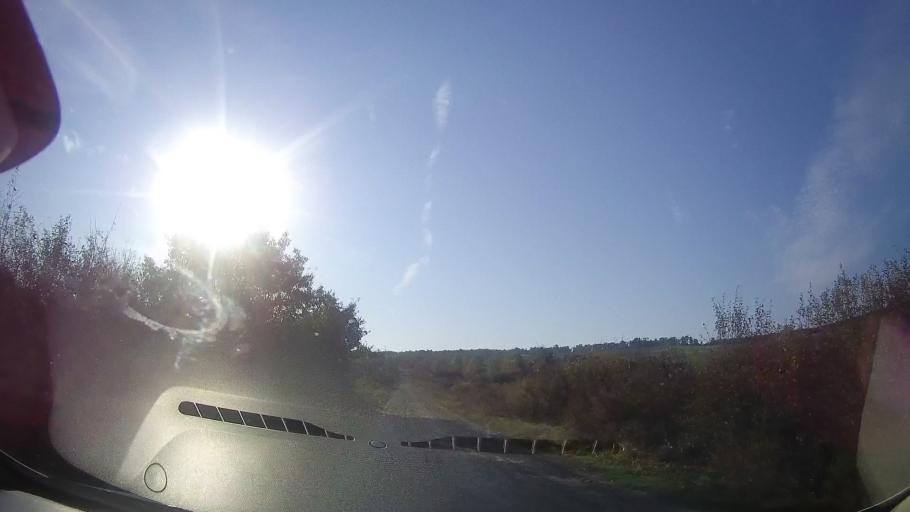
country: RO
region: Timis
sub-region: Comuna Bogda
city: Bogda
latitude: 45.9527
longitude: 21.6149
